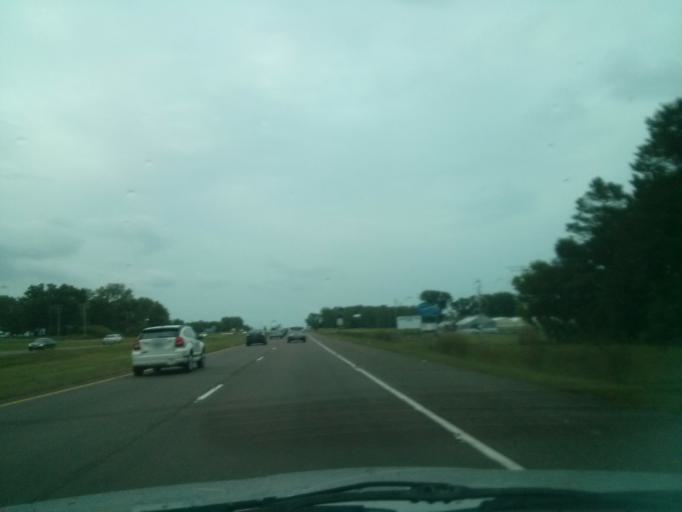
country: US
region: Minnesota
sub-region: Washington County
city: Lake Elmo
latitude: 45.0356
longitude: -92.8820
